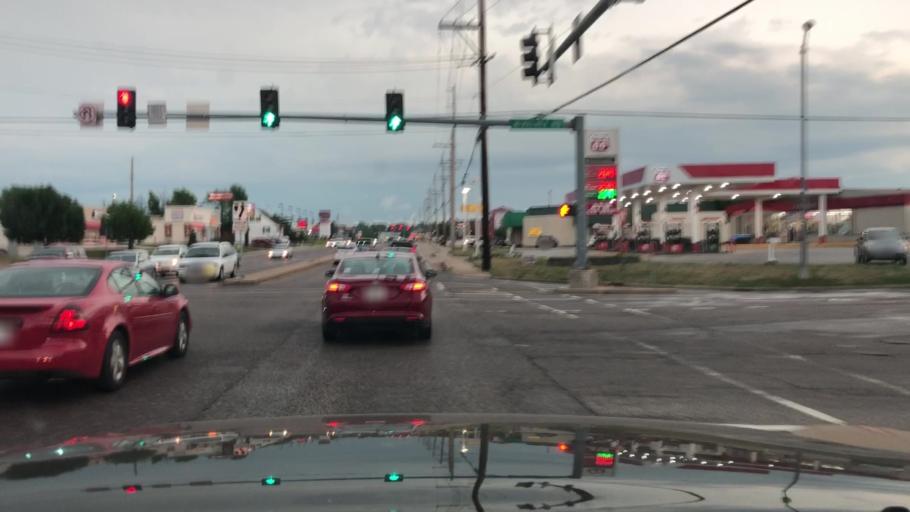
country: US
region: Missouri
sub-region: Saint Louis County
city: Bridgeton
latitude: 38.7512
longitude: -90.4265
